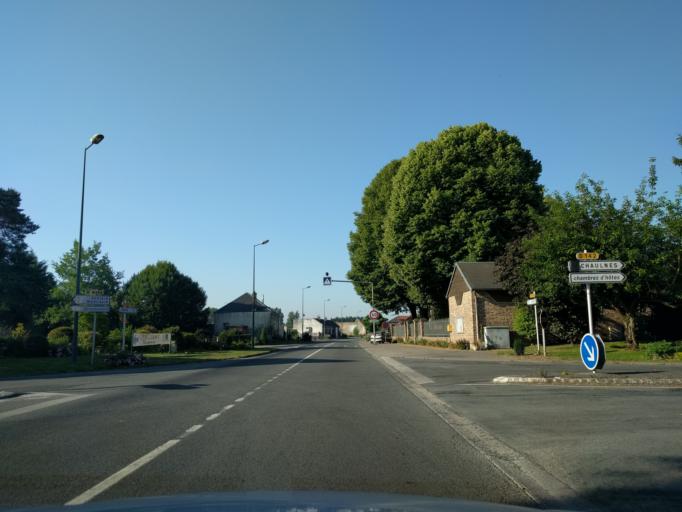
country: FR
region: Picardie
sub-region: Departement de la Somme
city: Chaulnes
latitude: 49.8098
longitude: 2.8467
